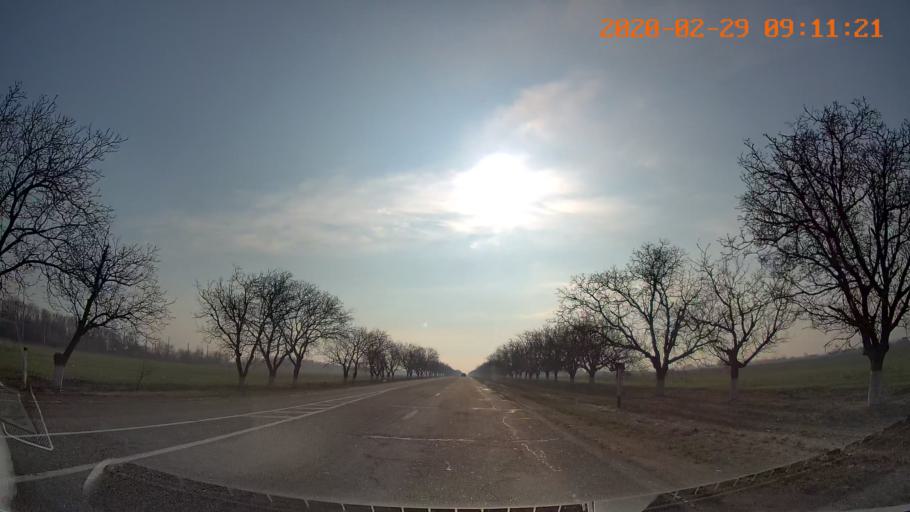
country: MD
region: Telenesti
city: Slobozia
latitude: 46.8359
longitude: 29.7983
